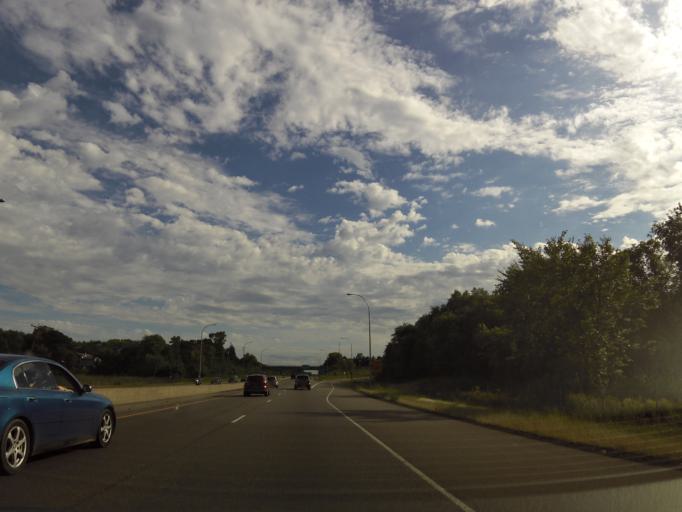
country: US
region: Minnesota
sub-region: Hennepin County
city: New Hope
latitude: 45.0722
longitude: -93.4017
